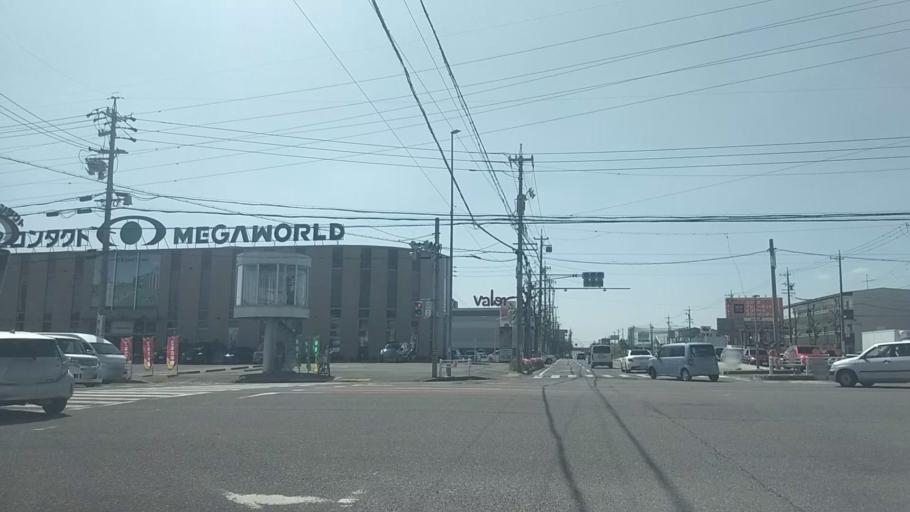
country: JP
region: Aichi
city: Okazaki
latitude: 34.9807
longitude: 137.1621
